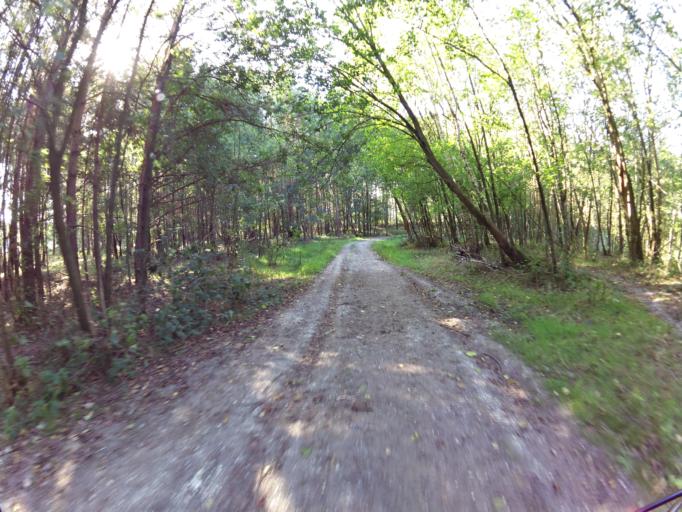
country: DE
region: North Rhine-Westphalia
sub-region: Regierungsbezirk Koln
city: Gangelt
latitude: 50.9765
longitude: 6.0168
